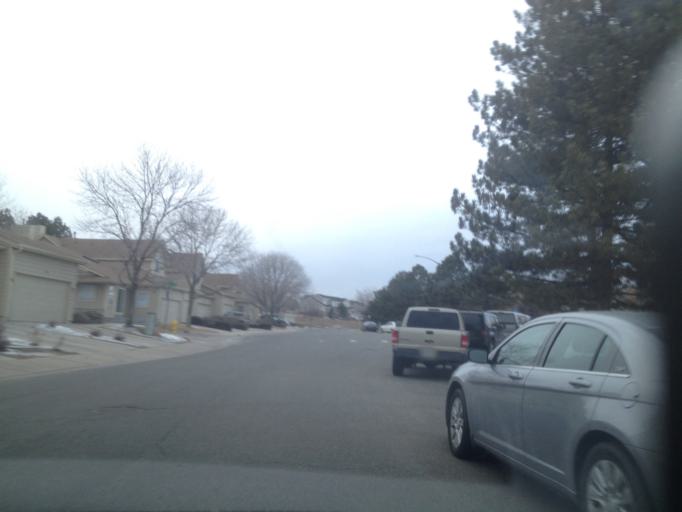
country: US
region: Colorado
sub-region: Adams County
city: Westminster
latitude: 39.8172
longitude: -105.0508
